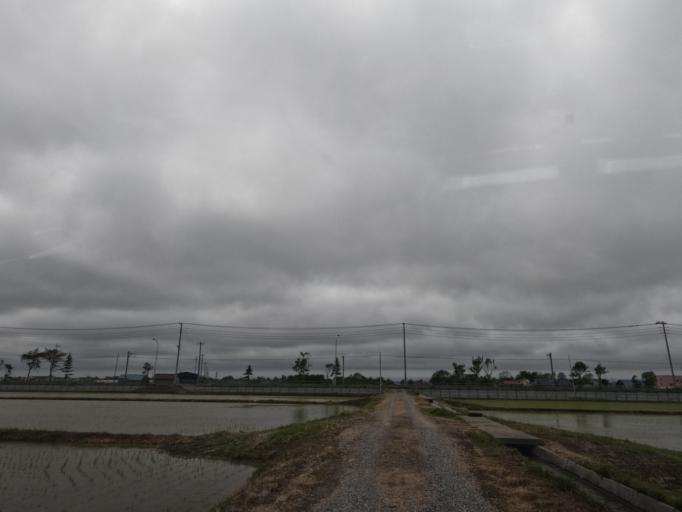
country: JP
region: Hokkaido
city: Tobetsu
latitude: 43.2440
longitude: 141.5178
